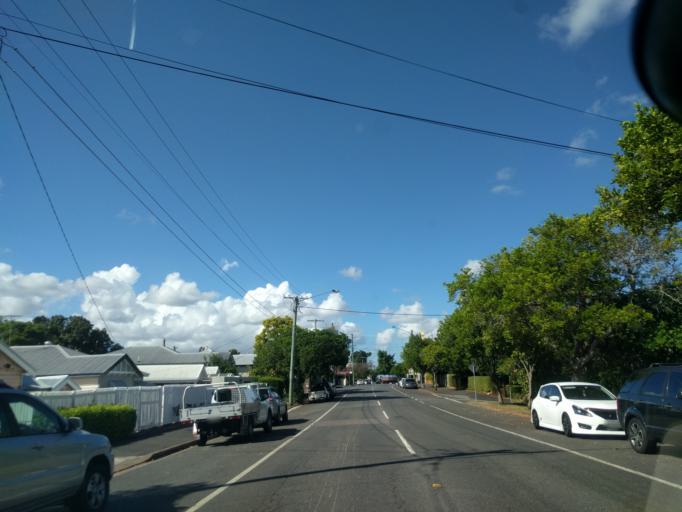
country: AU
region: Queensland
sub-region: Brisbane
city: Milton
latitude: -27.4551
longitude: 153.0025
